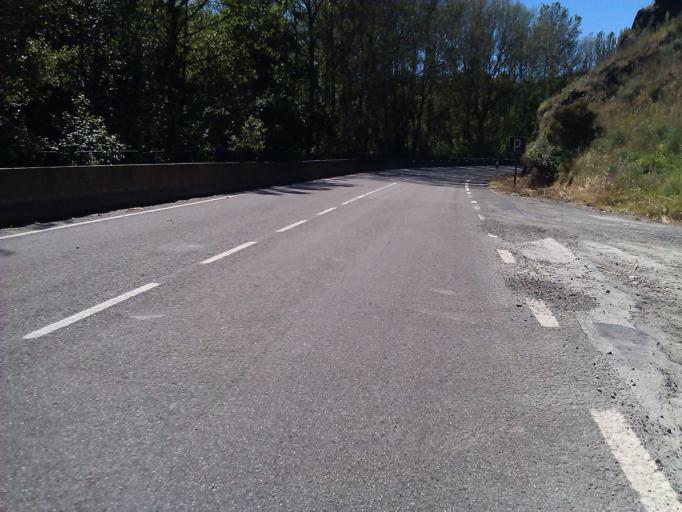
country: ES
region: Castille and Leon
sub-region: Provincia de Leon
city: Trabadelo
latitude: 42.6568
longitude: -6.9069
